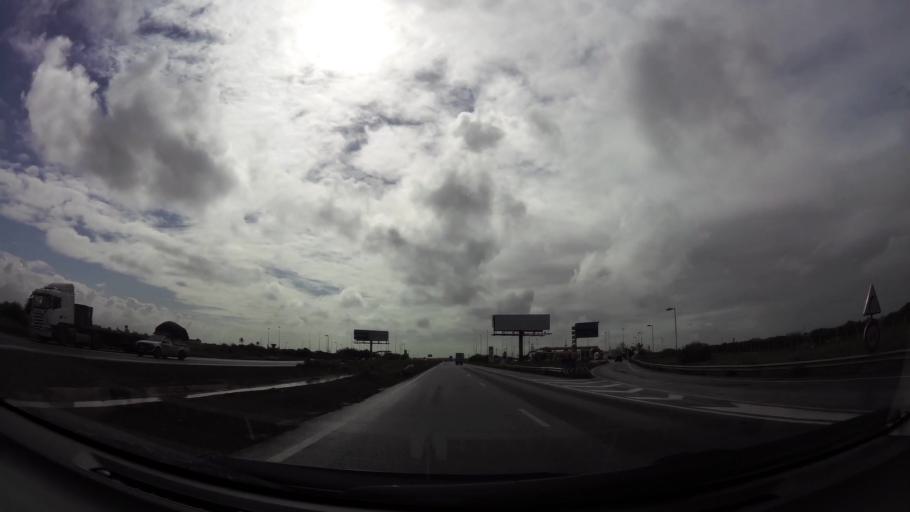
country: MA
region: Grand Casablanca
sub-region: Nouaceur
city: Dar Bouazza
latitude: 33.3534
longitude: -7.9764
